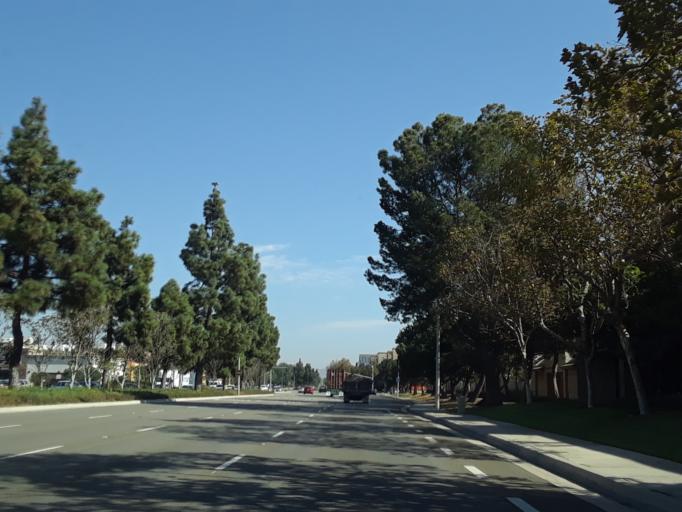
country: US
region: California
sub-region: Orange County
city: Irvine
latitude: 33.6866
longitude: -117.8337
